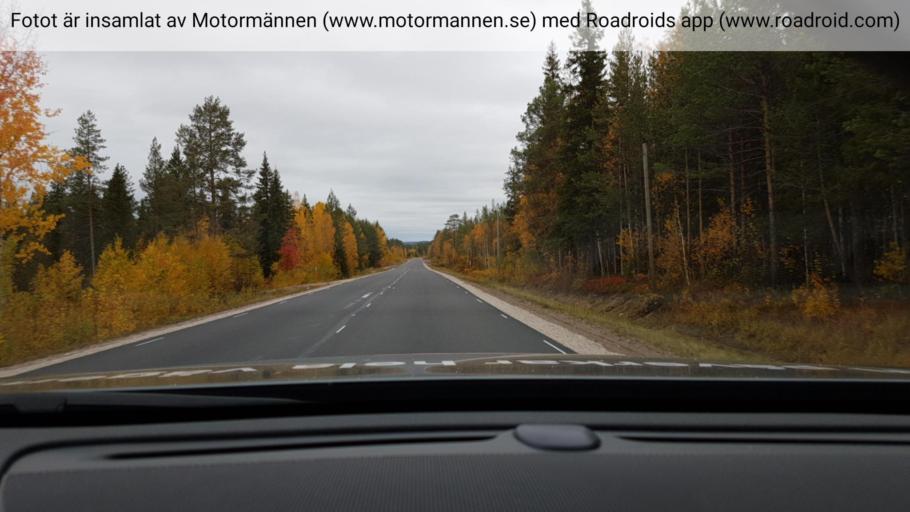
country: SE
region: Norrbotten
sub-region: Overkalix Kommun
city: OEverkalix
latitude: 66.3788
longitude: 22.8351
